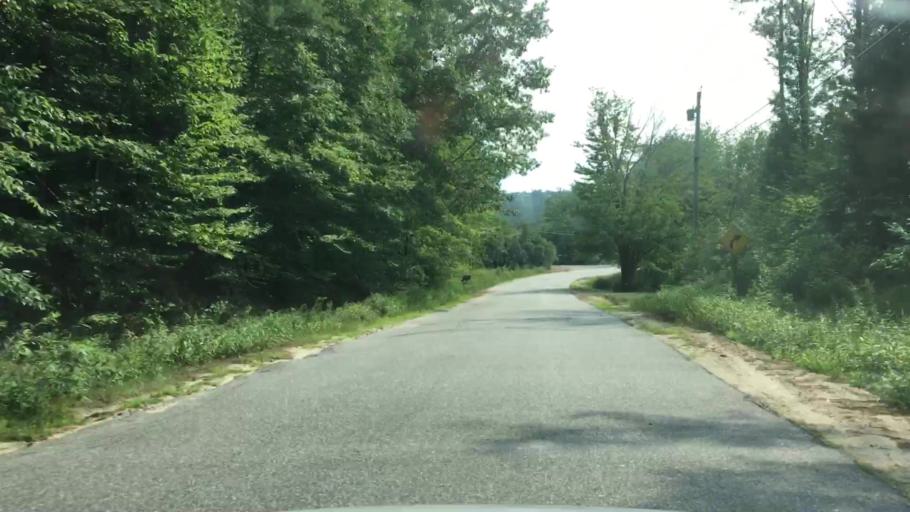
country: US
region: Maine
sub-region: Oxford County
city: Buckfield
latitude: 44.2879
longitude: -70.3468
